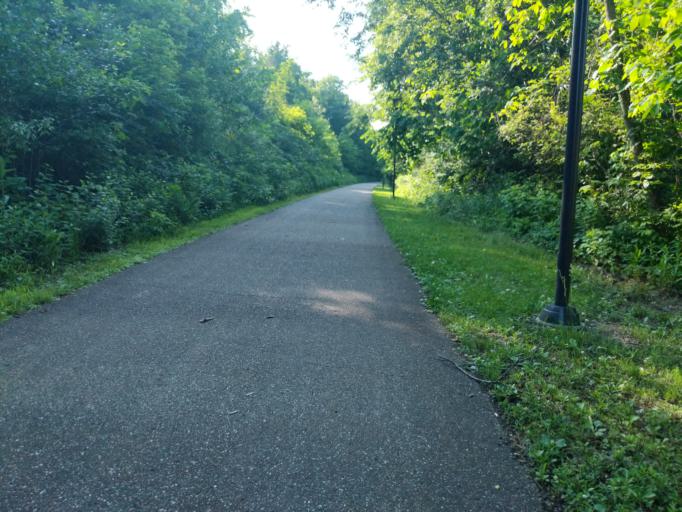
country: US
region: Ohio
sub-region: Athens County
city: Nelsonville
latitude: 39.4337
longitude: -82.2138
